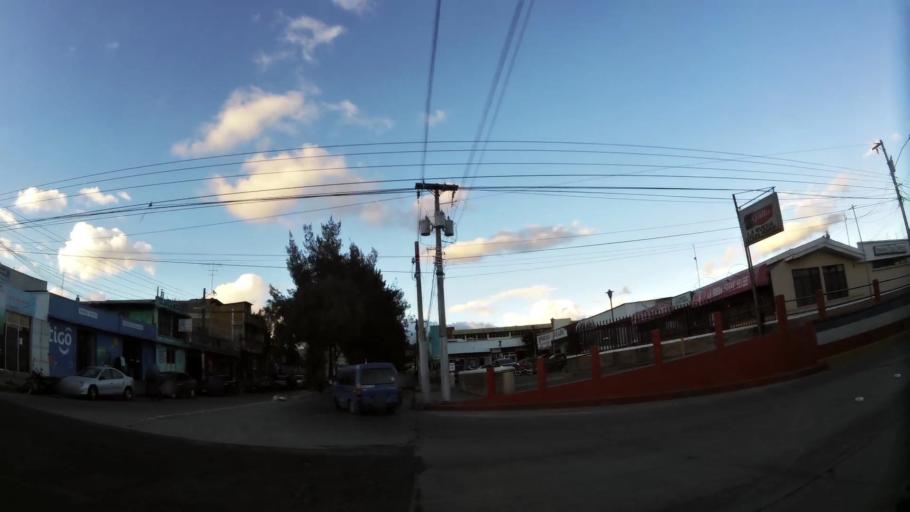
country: GT
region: Quetzaltenango
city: Quetzaltenango
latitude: 14.8437
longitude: -91.5152
